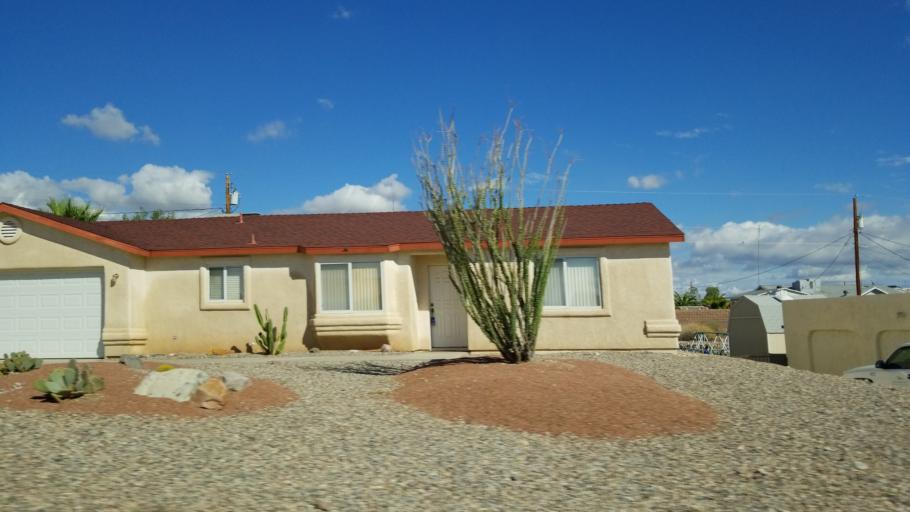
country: US
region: Arizona
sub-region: Mohave County
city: Lake Havasu City
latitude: 34.4771
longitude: -114.2672
